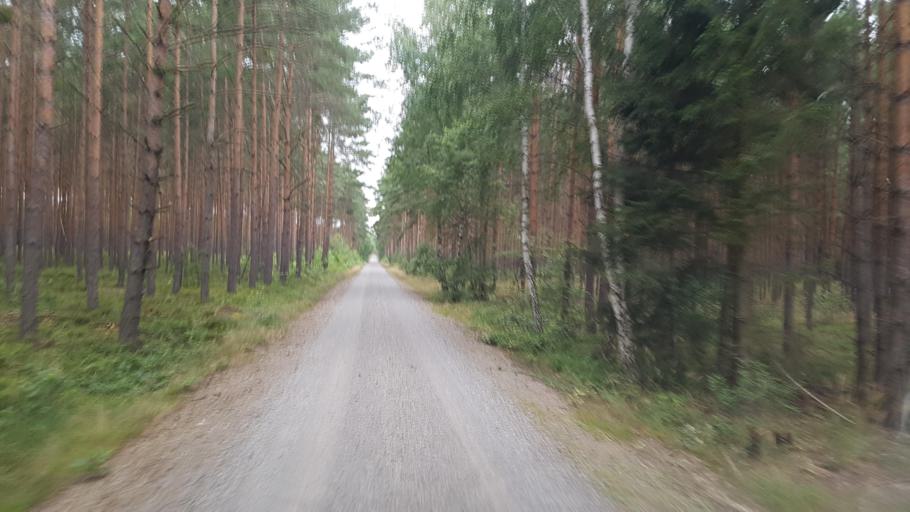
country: DE
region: Brandenburg
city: Schonborn
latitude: 51.6120
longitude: 13.5046
